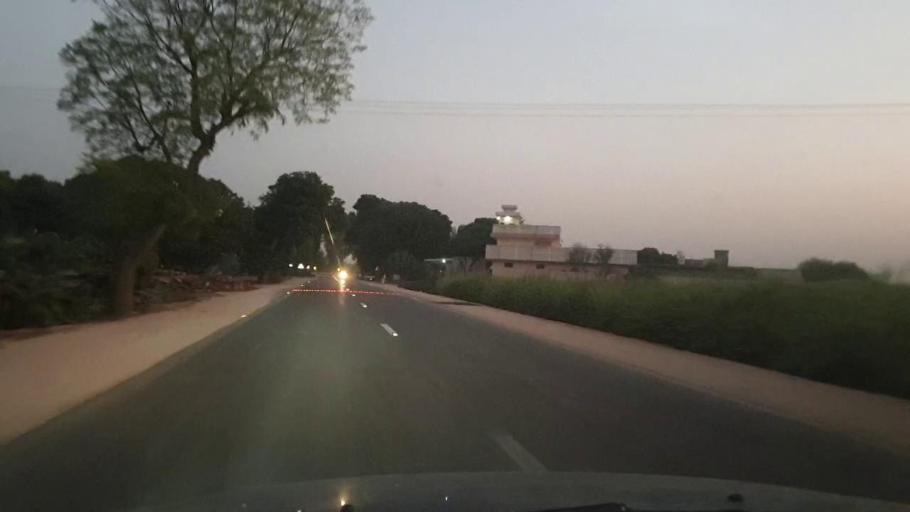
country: PK
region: Sindh
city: Tando Allahyar
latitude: 25.4203
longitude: 68.7542
